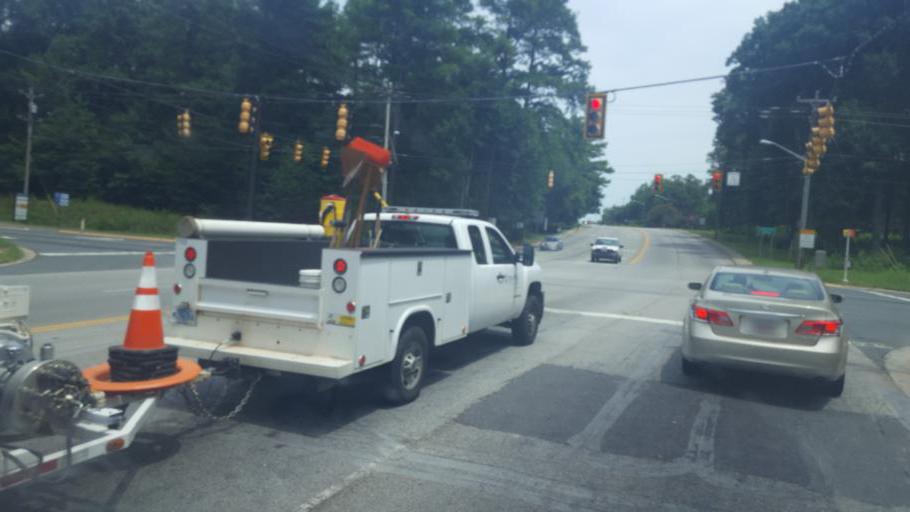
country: US
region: South Carolina
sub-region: York County
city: Rock Hill
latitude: 34.9406
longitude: -81.0602
